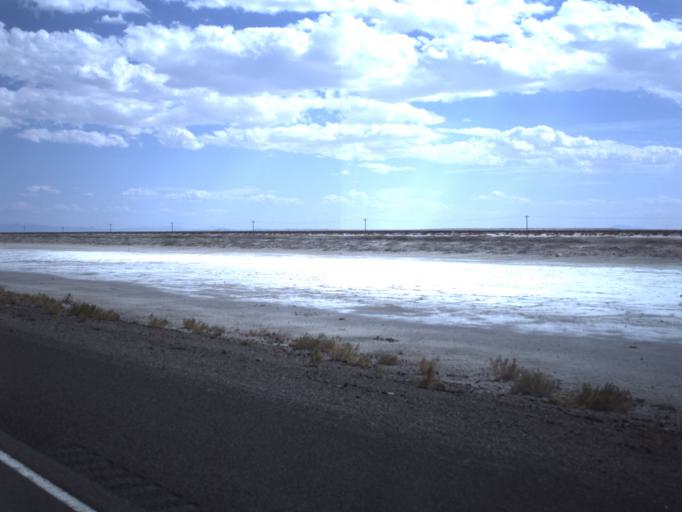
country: US
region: Utah
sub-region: Tooele County
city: Wendover
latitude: 40.7375
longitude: -113.8050
